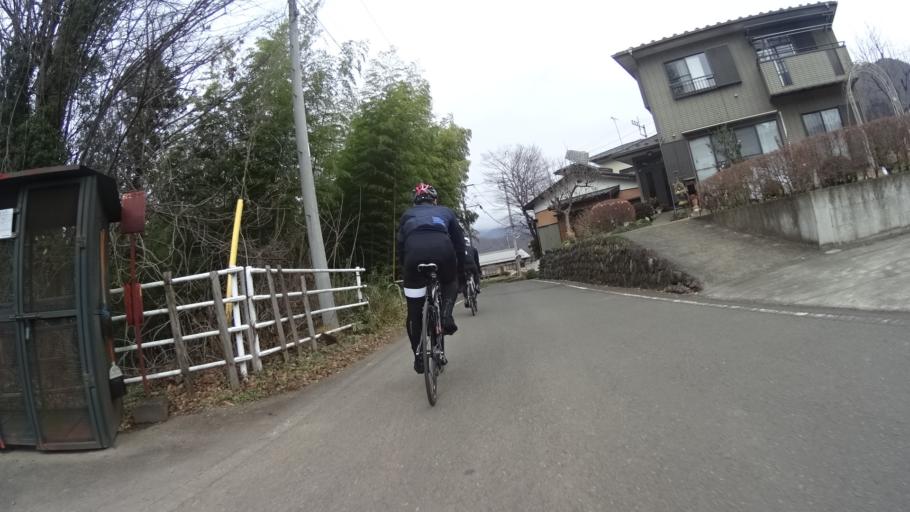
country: JP
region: Yamanashi
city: Otsuki
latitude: 35.5872
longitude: 138.9297
